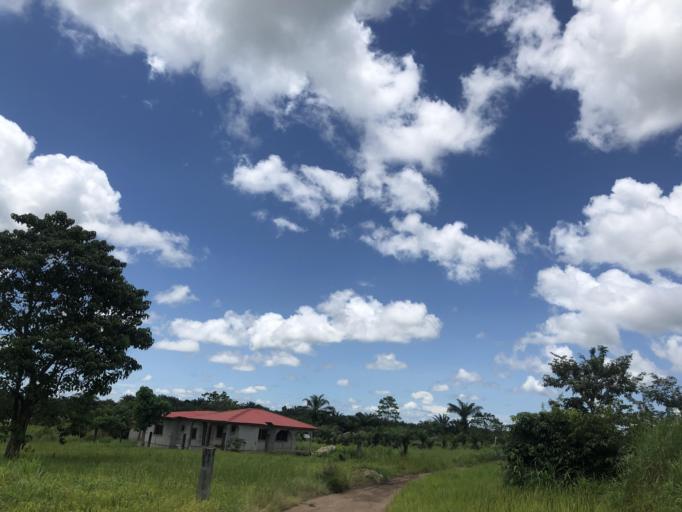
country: SL
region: Northern Province
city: Makeni
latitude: 8.8499
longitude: -12.0618
